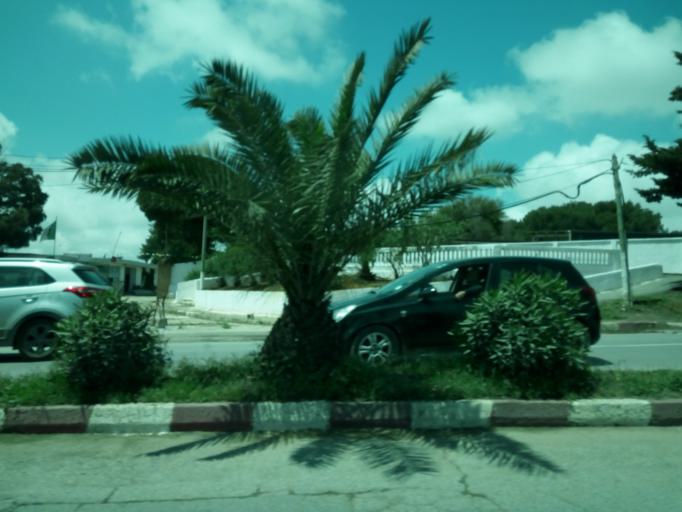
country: DZ
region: Tipaza
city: Saoula
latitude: 36.7274
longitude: 2.9910
